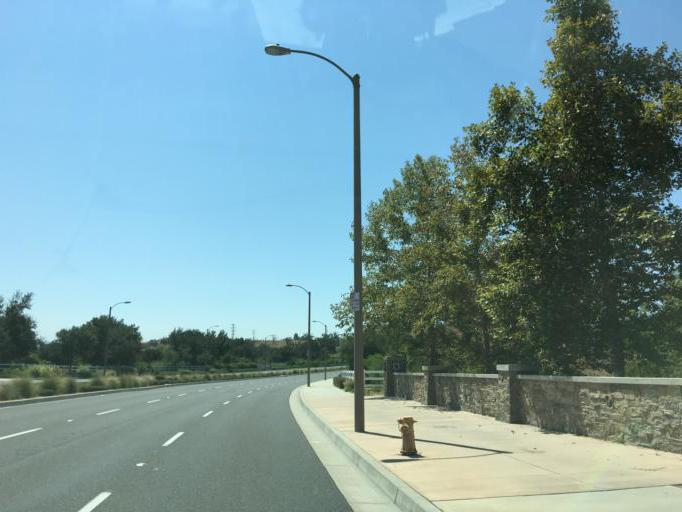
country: US
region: California
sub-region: Los Angeles County
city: Santa Clarita
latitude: 34.4041
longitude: -118.5775
